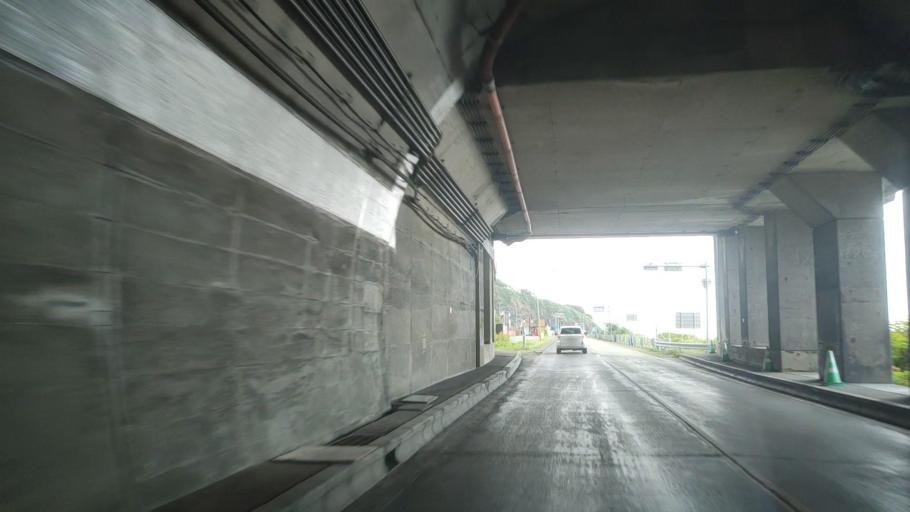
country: JP
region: Hokkaido
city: Rumoi
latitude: 43.7897
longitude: 141.3721
